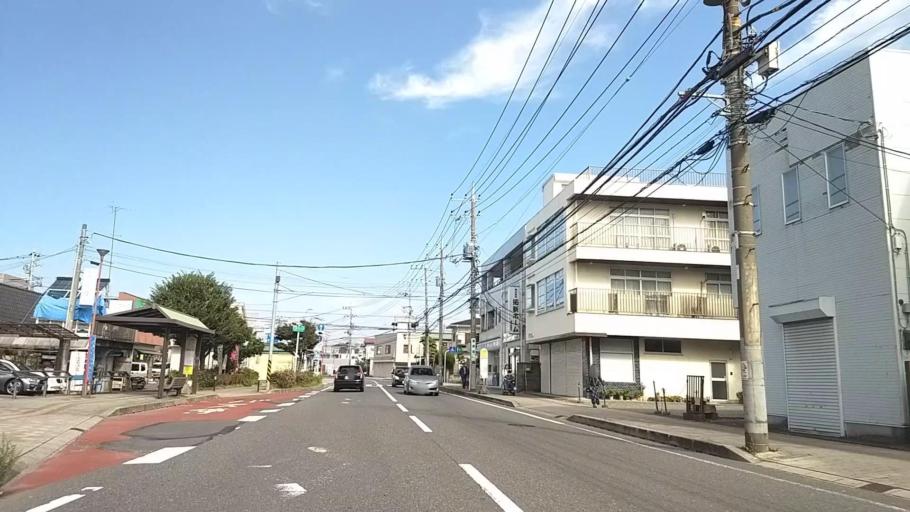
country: JP
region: Kanagawa
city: Atsugi
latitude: 35.4468
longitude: 139.3612
